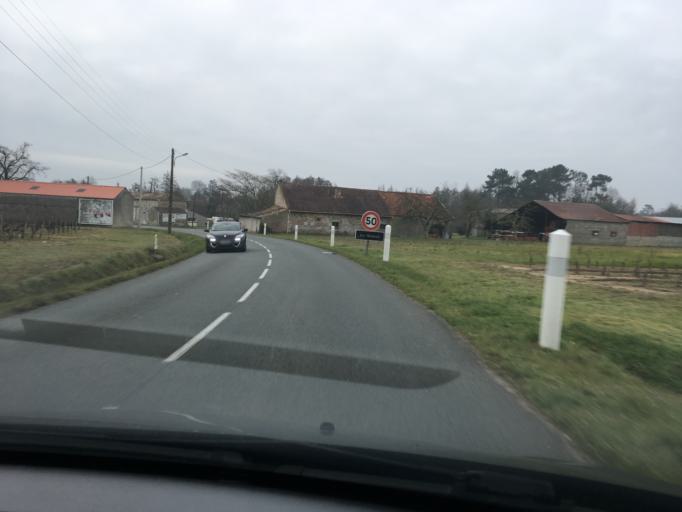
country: FR
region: Aquitaine
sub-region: Departement de la Gironde
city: Saint-Ciers-sur-Gironde
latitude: 45.2759
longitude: -0.5974
